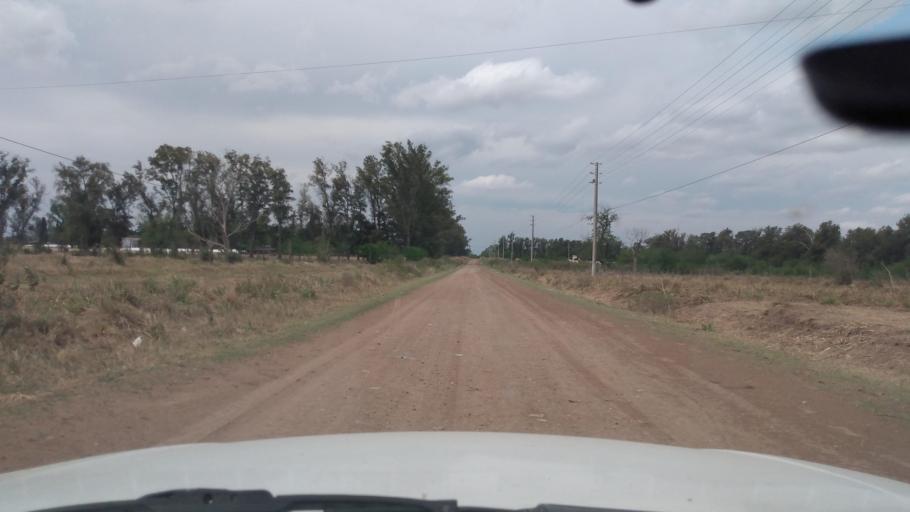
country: AR
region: Buenos Aires
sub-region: Partido de Lujan
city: Lujan
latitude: -34.5560
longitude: -59.1789
